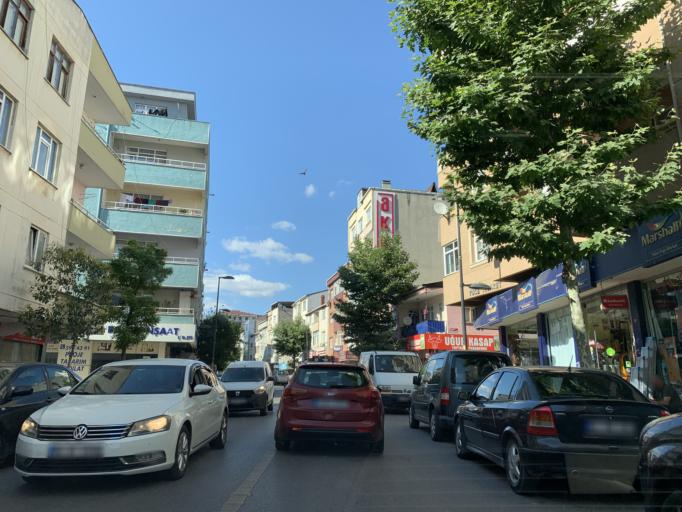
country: TR
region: Istanbul
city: Pendik
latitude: 40.8752
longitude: 29.2695
